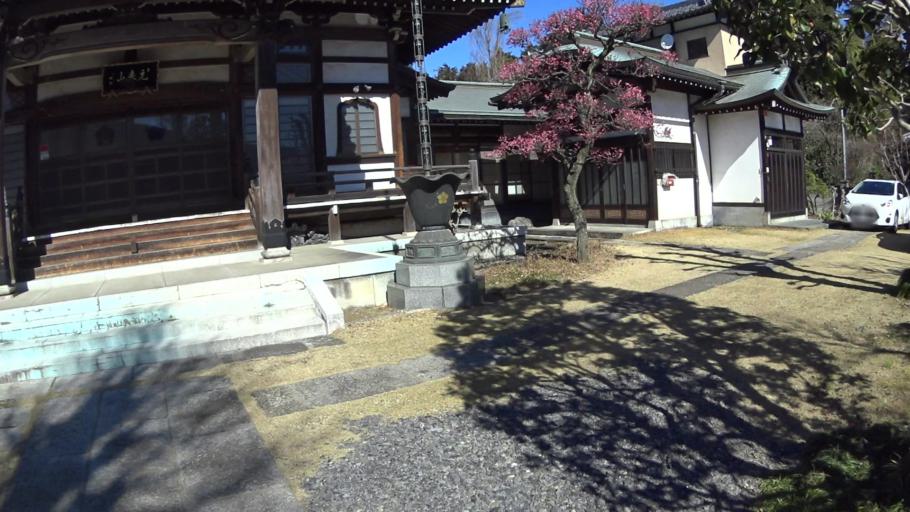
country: JP
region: Saitama
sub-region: Kawaguchi-shi
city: Hatogaya-honcho
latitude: 35.8518
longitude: 139.7536
